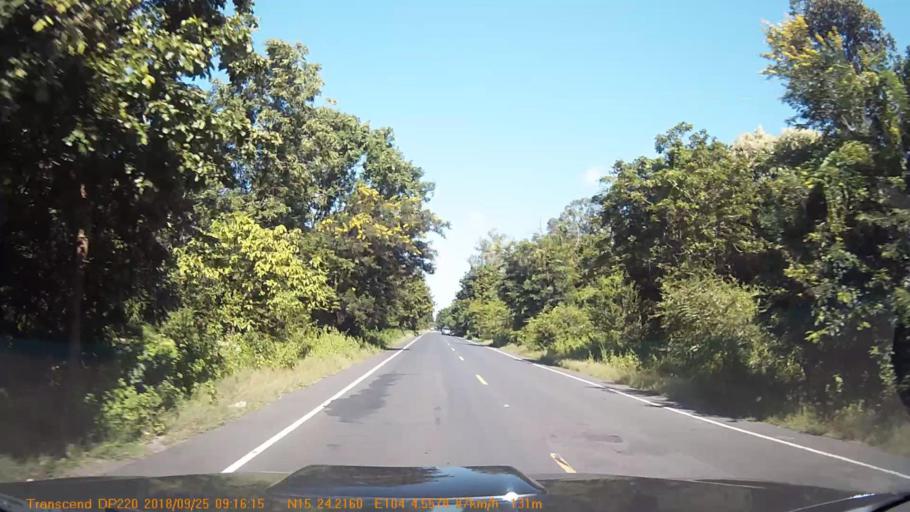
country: TH
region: Sisaket
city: Sila Lat
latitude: 15.4034
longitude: 104.0762
